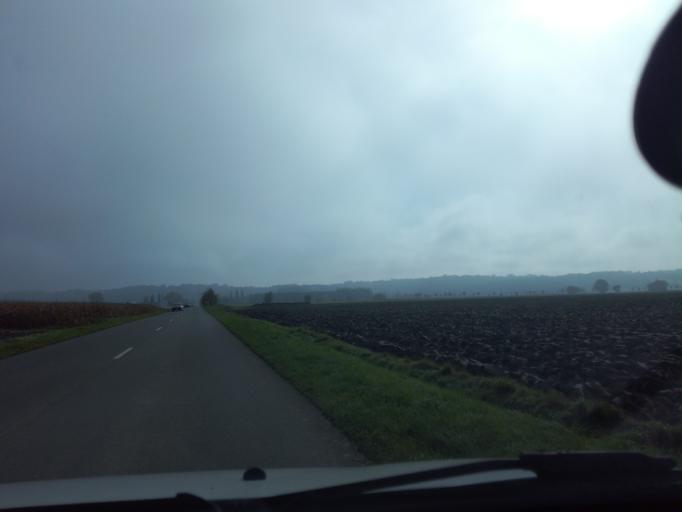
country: FR
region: Brittany
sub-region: Departement d'Ille-et-Vilaine
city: Saint-Broladre
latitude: 48.5968
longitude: -1.6739
